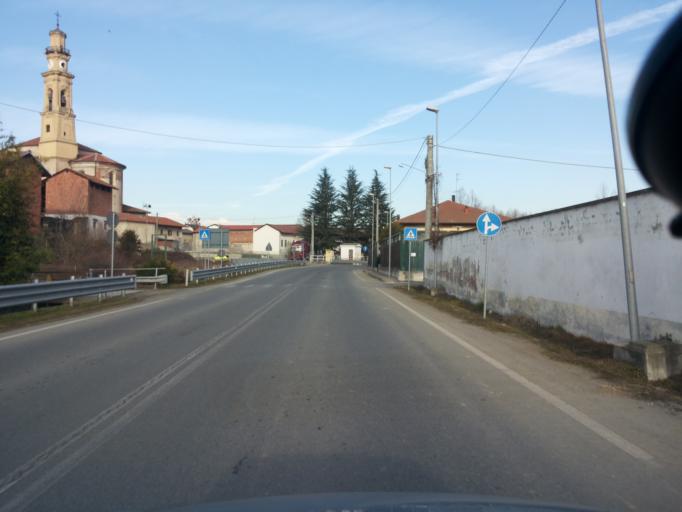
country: IT
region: Piedmont
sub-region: Provincia di Vercelli
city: Arborio
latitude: 45.4958
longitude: 8.3913
